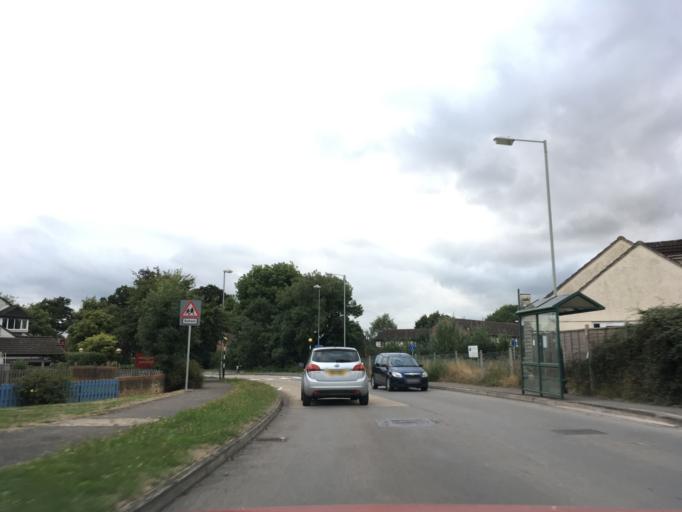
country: GB
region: England
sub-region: Wiltshire
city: Chippenham
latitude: 51.4482
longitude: -2.1019
